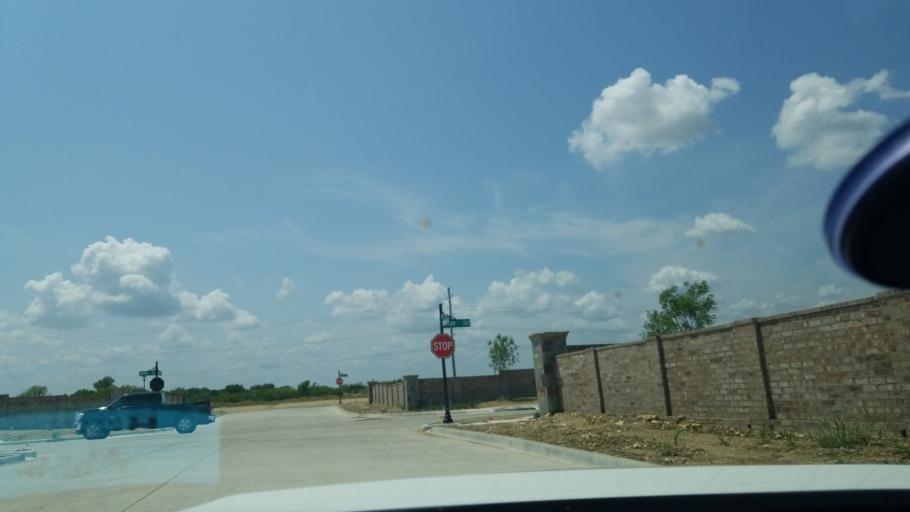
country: US
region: Texas
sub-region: Tarrant County
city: Haslet
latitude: 32.9413
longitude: -97.3967
